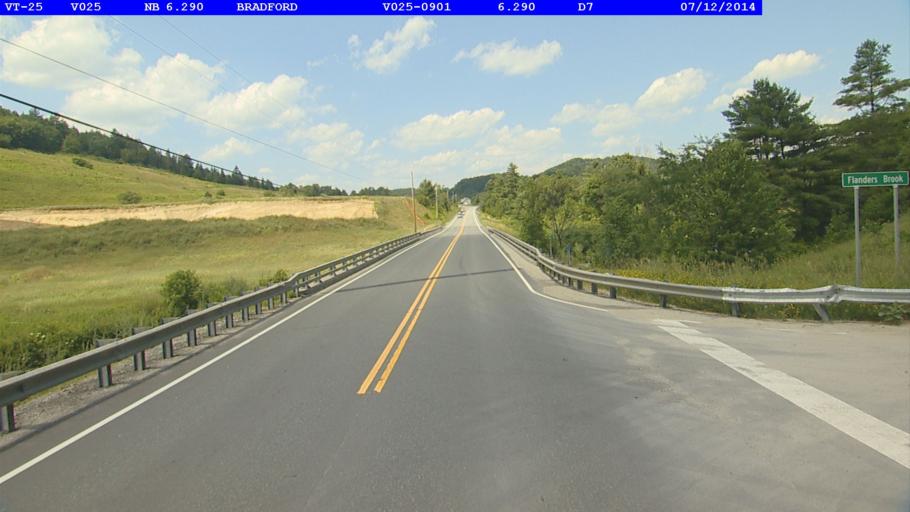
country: US
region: New Hampshire
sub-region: Grafton County
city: Haverhill
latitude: 44.0332
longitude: -72.1951
